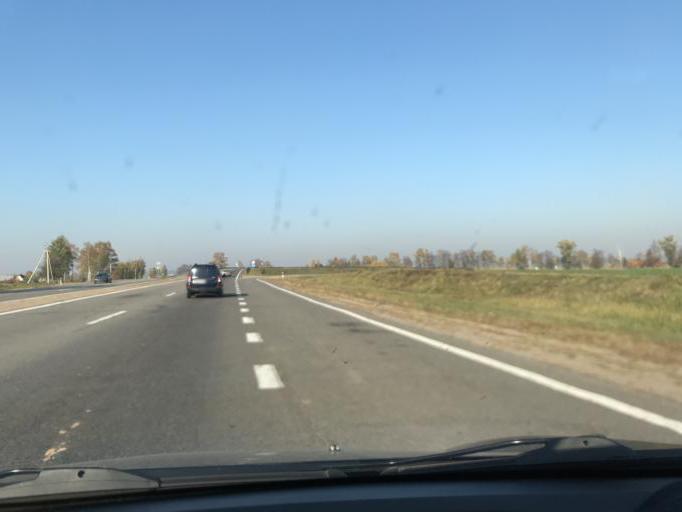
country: BY
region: Minsk
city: Luhavaya Slabada
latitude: 53.7870
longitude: 27.8214
